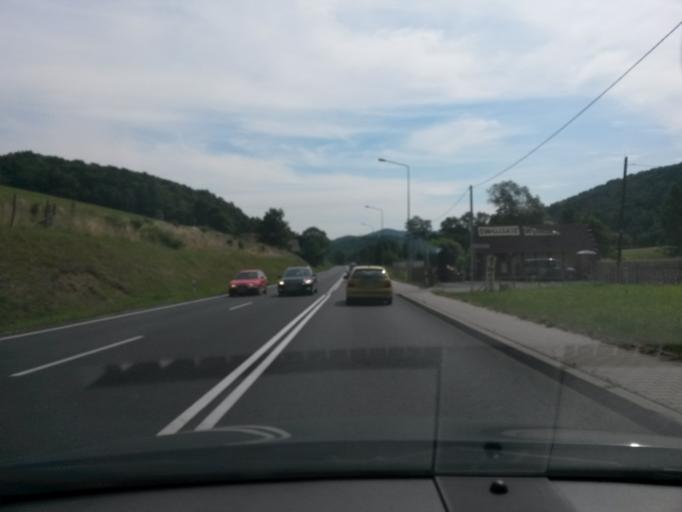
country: PL
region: Lower Silesian Voivodeship
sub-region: Powiat jeleniogorski
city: Janowice Wielkie
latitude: 50.9085
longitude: 15.9418
